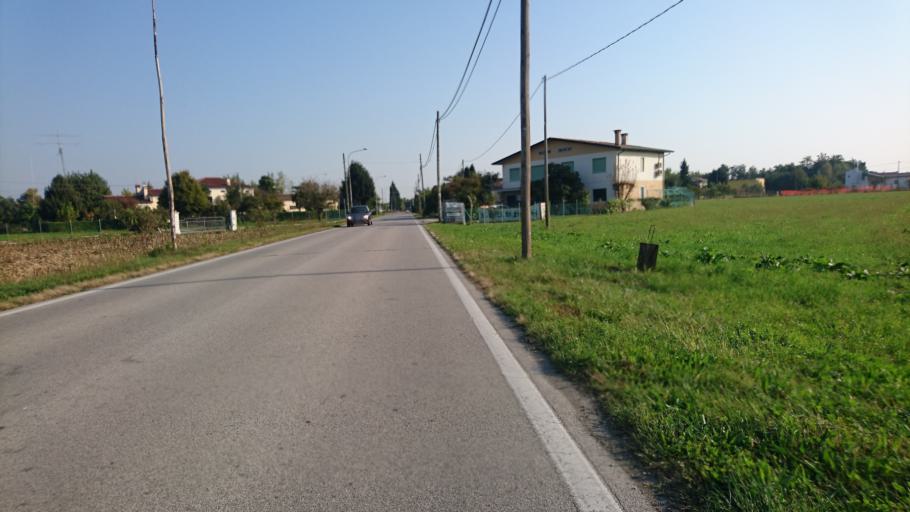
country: IT
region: Veneto
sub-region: Provincia di Padova
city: Grantorto
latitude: 45.5978
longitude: 11.7219
